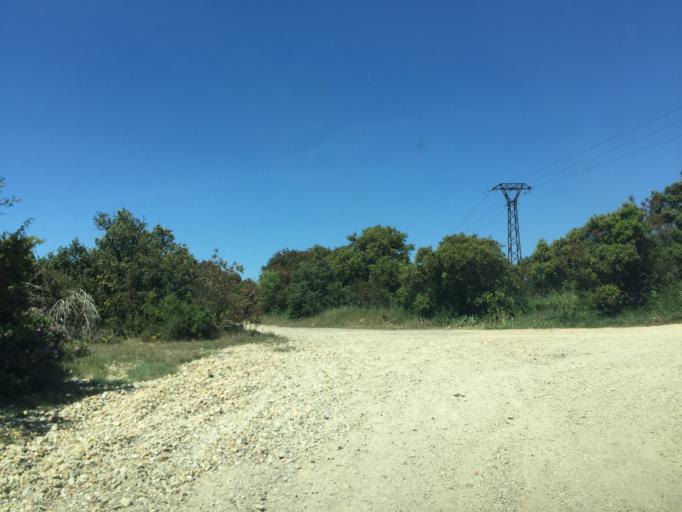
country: FR
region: Provence-Alpes-Cote d'Azur
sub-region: Departement du Vaucluse
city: Chateauneuf-du-Pape
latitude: 44.0548
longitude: 4.8124
